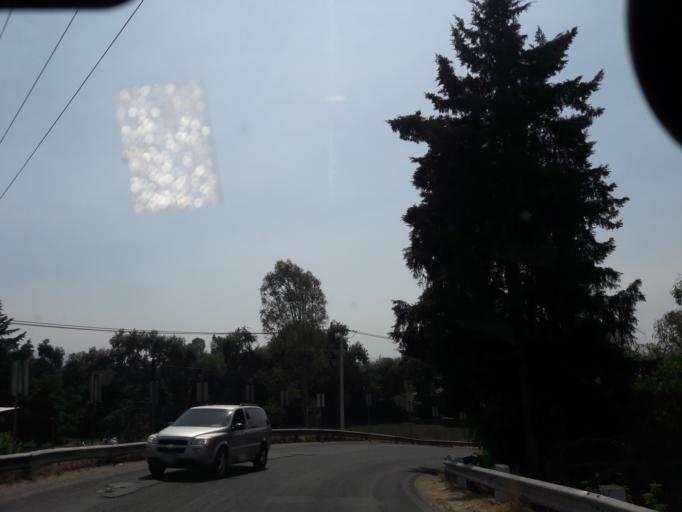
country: MX
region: Tlaxcala
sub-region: Ixtacuixtla de Mariano Matamoros
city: Villa Mariano Matamoros
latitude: 19.3150
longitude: -98.3877
